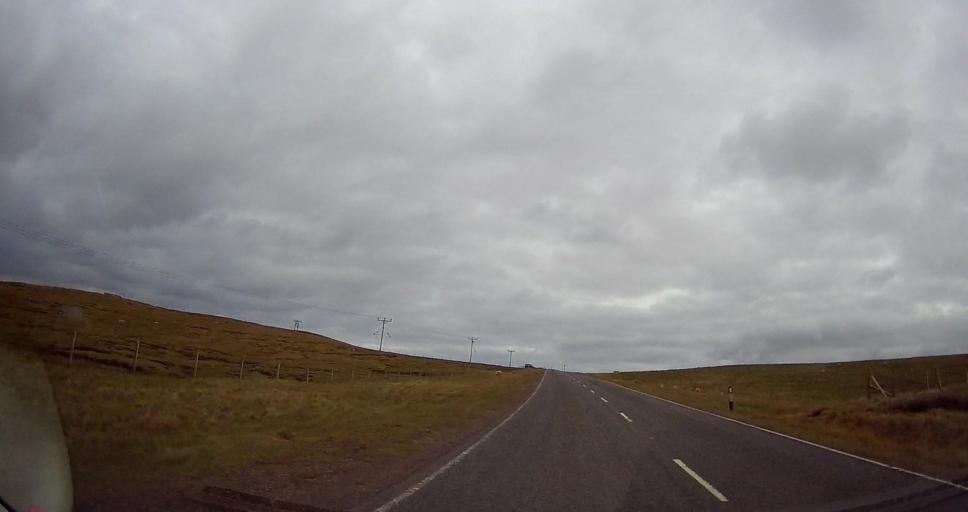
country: GB
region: Scotland
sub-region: Shetland Islands
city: Shetland
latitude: 60.6547
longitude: -1.0682
